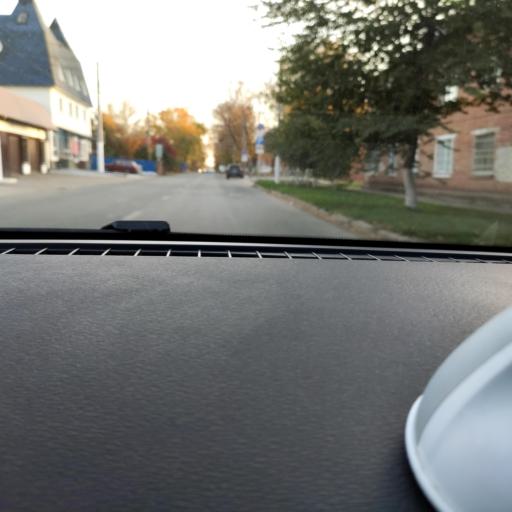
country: RU
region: Samara
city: Samara
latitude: 53.2298
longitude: 50.2355
